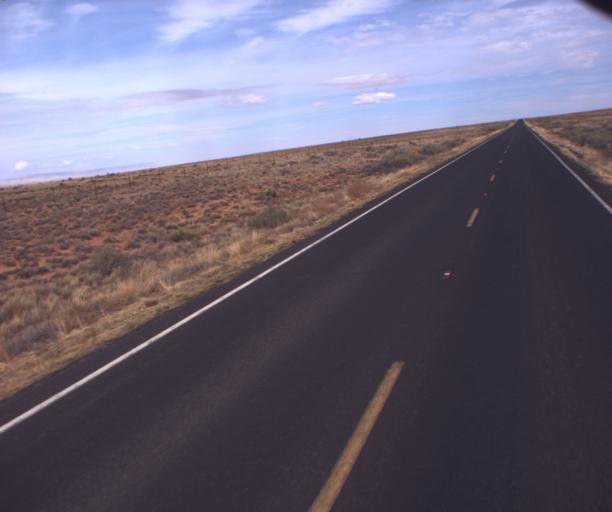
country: US
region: Arizona
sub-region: Apache County
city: Ganado
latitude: 35.8524
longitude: -109.5982
